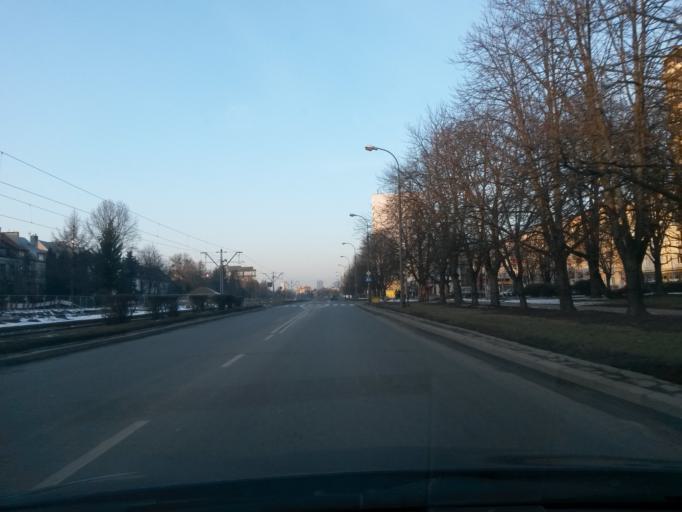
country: PL
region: Masovian Voivodeship
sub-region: Warszawa
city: Mokotow
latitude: 52.1916
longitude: 21.0020
